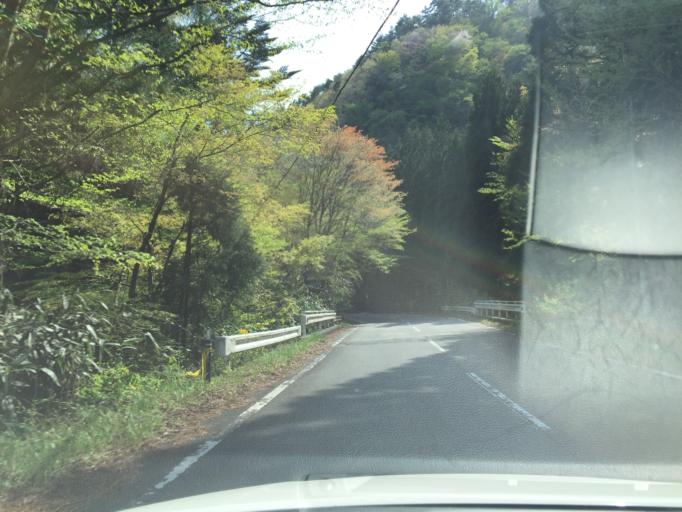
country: JP
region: Fukushima
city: Iwaki
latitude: 37.1763
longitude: 140.8517
